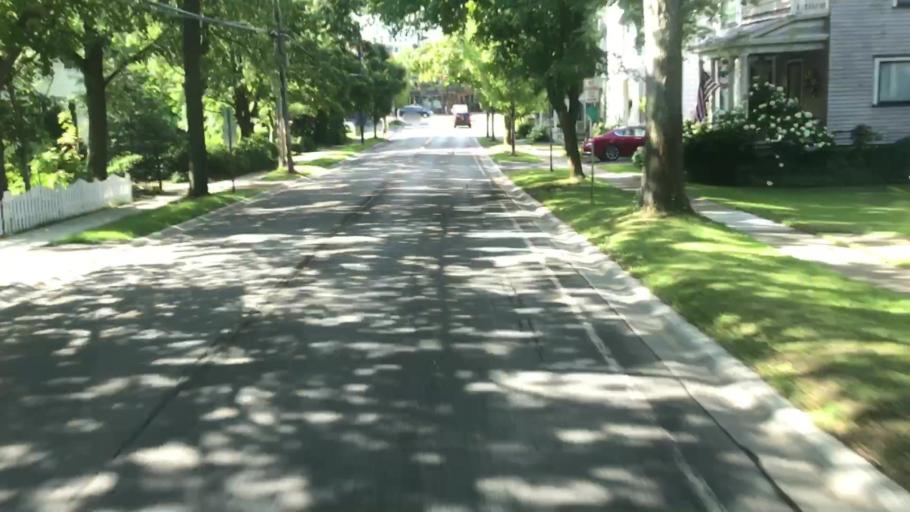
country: US
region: New York
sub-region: Onondaga County
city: Skaneateles
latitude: 42.9469
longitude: -76.4275
